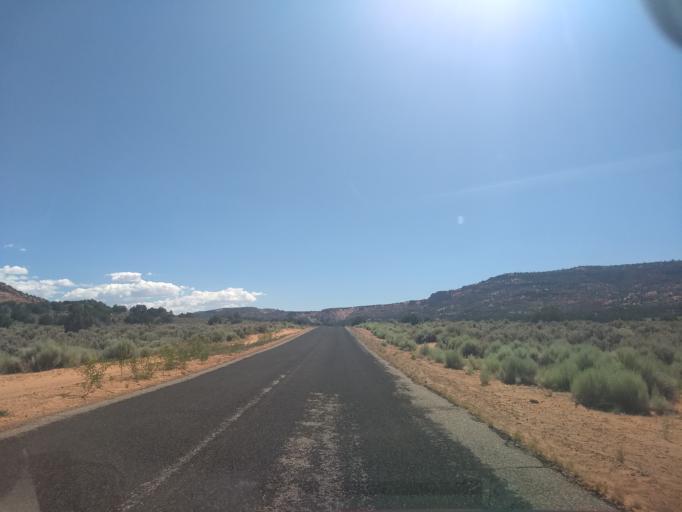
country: US
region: Utah
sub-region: Washington County
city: Hildale
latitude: 37.0163
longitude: -112.8388
